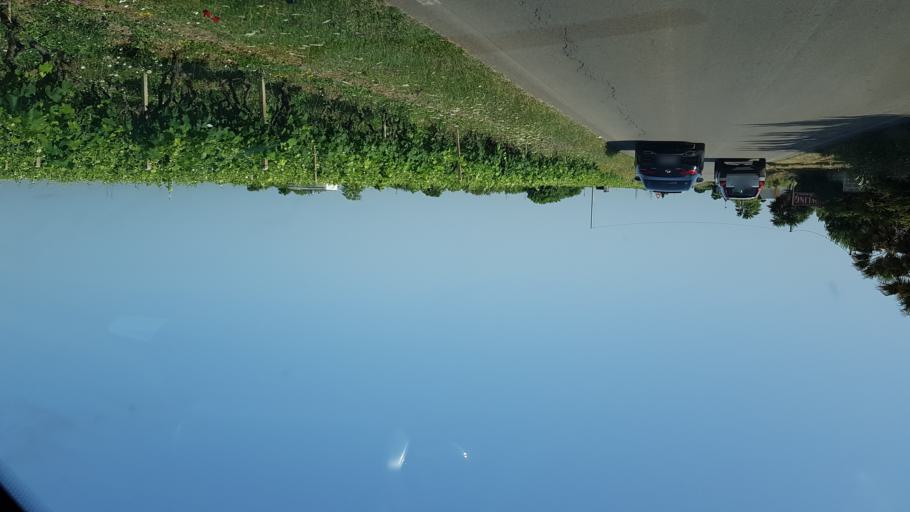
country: IT
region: Apulia
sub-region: Provincia di Brindisi
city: San Pancrazio Salentino
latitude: 40.4018
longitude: 17.8355
